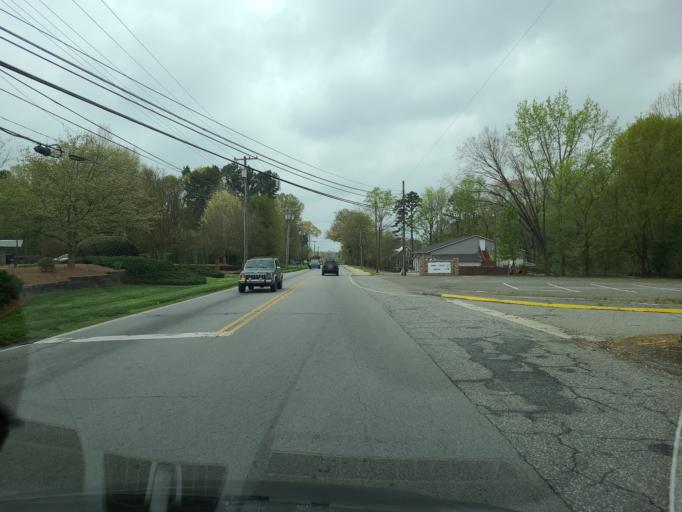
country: US
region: North Carolina
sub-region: Lincoln County
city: Lincolnton
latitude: 35.4921
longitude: -81.2490
